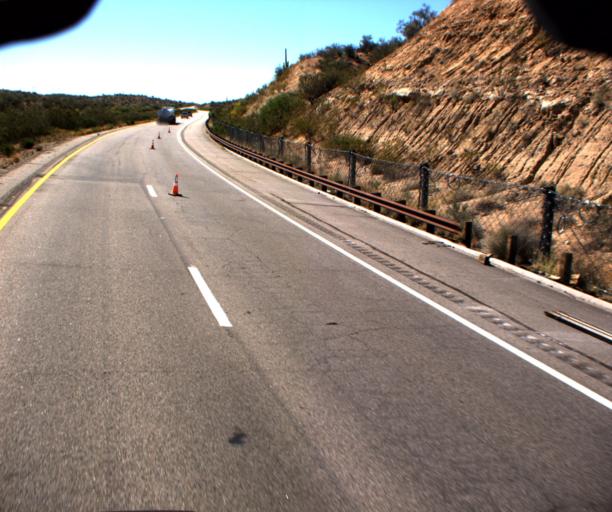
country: US
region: Arizona
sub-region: Yavapai County
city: Bagdad
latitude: 34.3664
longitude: -113.1778
